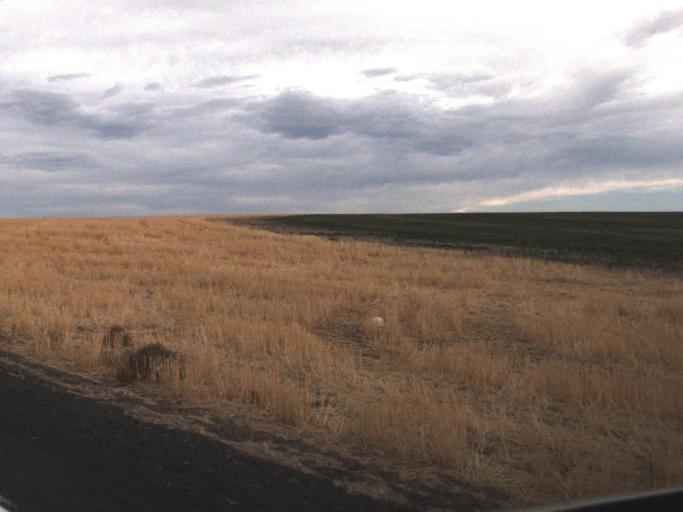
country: US
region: Washington
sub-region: Okanogan County
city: Coulee Dam
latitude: 47.6316
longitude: -118.7208
